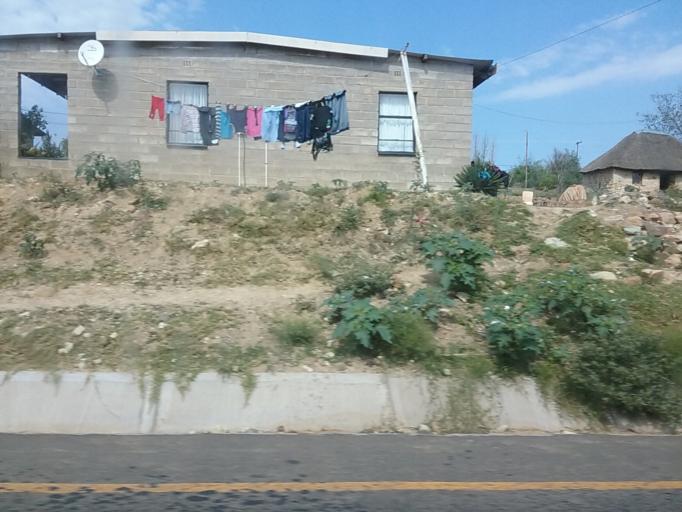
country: LS
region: Berea
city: Teyateyaneng
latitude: -29.1284
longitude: 27.9839
